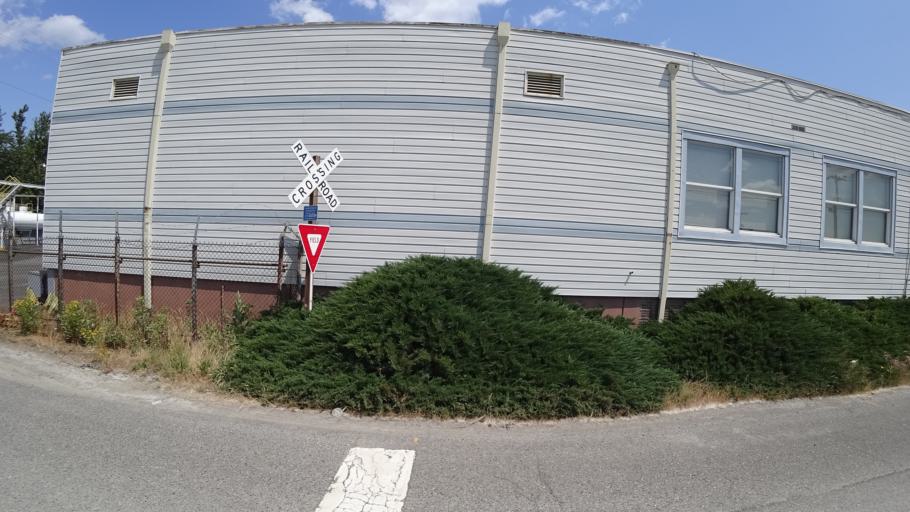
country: US
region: Washington
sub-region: Clark County
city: Vancouver
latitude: 45.6154
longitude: -122.7131
